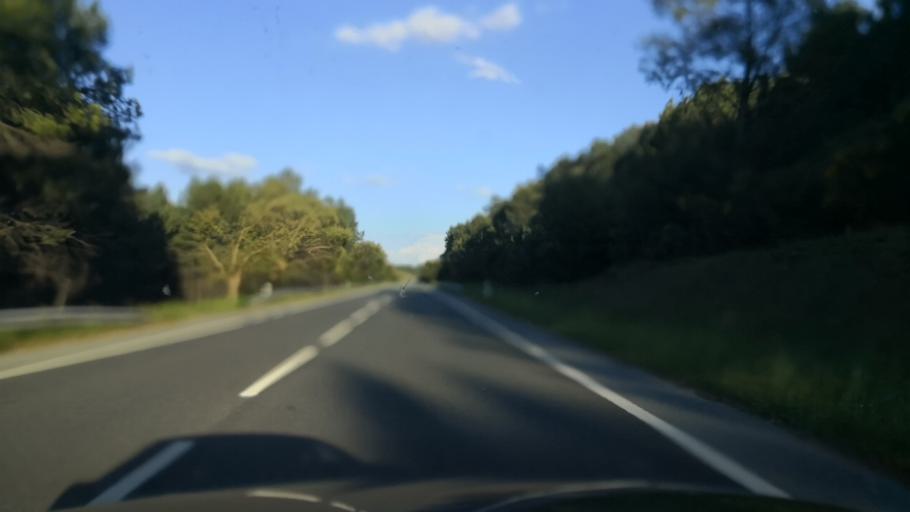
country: PT
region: Portalegre
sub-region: Marvao
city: Marvao
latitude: 39.3744
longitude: -7.3584
